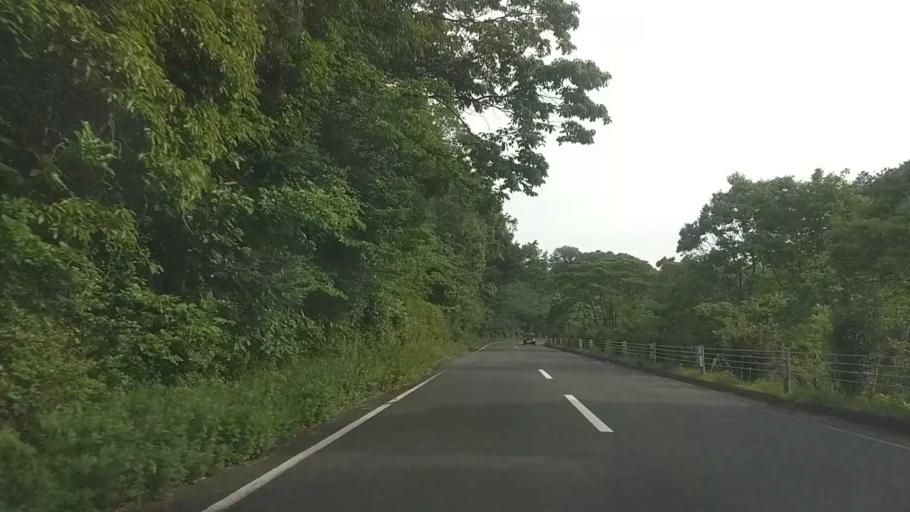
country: JP
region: Shizuoka
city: Kosai-shi
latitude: 34.7530
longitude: 137.6116
